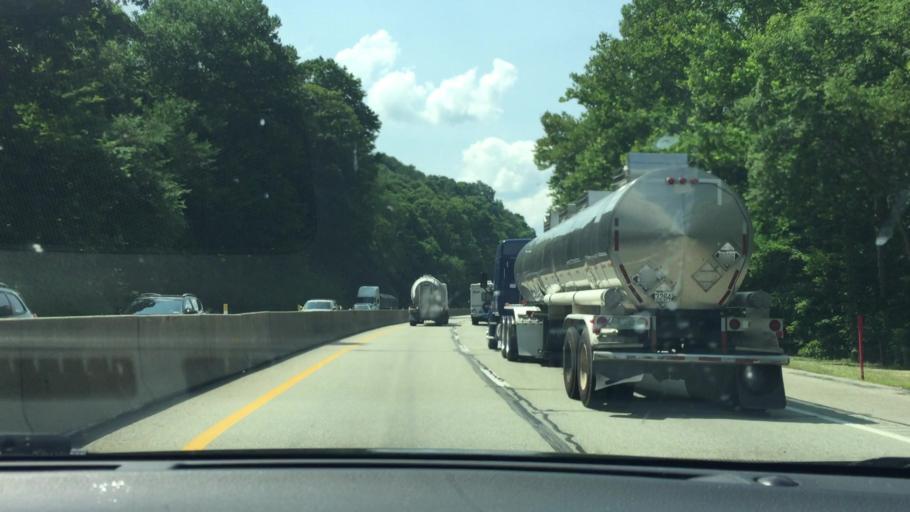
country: US
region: Pennsylvania
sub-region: Westmoreland County
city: Level Green
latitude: 40.4055
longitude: -79.7156
